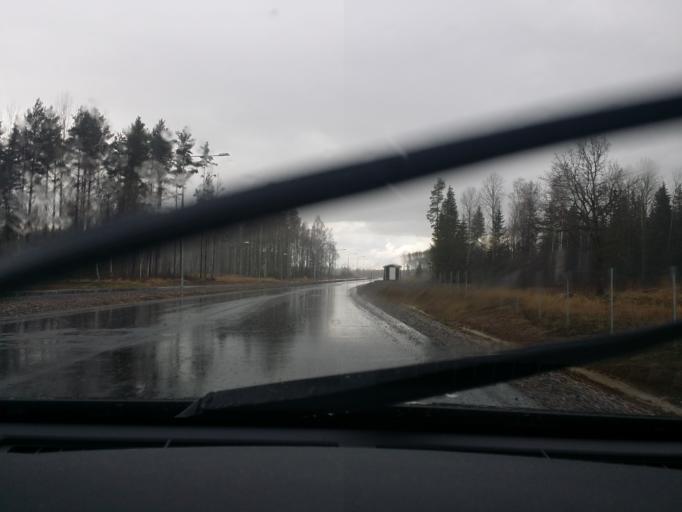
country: SE
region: Soedermanland
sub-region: Eskilstuna Kommun
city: Arla
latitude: 59.3570
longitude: 16.7006
